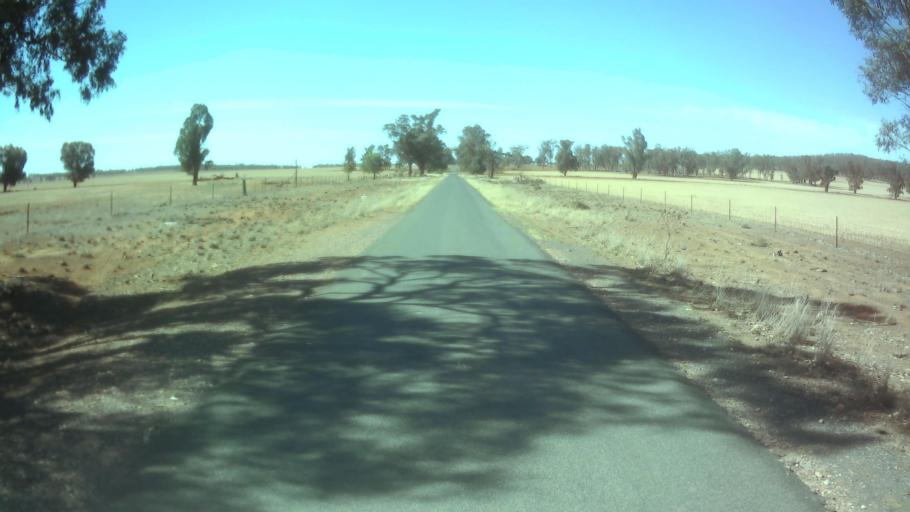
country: AU
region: New South Wales
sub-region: Forbes
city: Forbes
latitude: -33.7368
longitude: 147.7416
